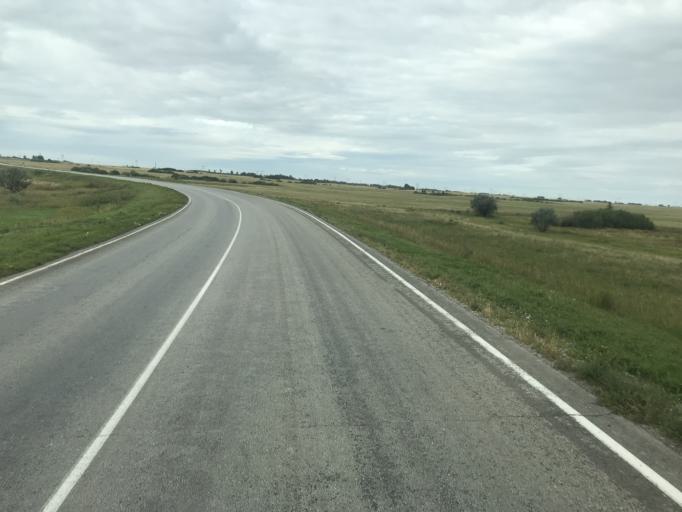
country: RU
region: Chelyabinsk
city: Bobrovka
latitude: 53.9862
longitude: 61.7000
